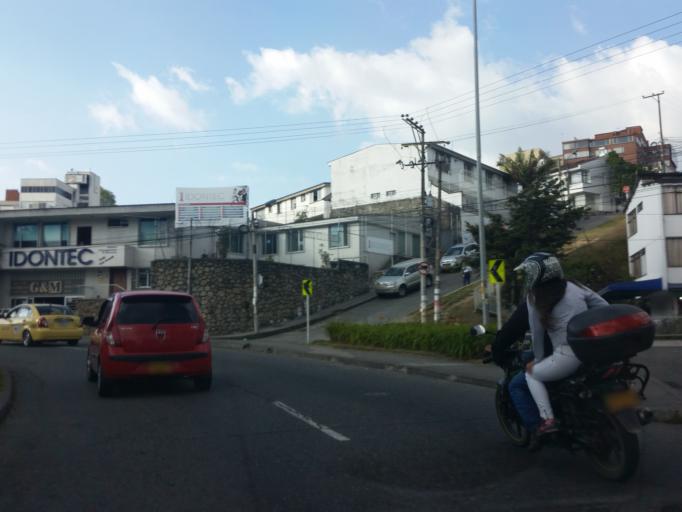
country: CO
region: Caldas
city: Villamaria
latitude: 5.0591
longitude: -75.4908
